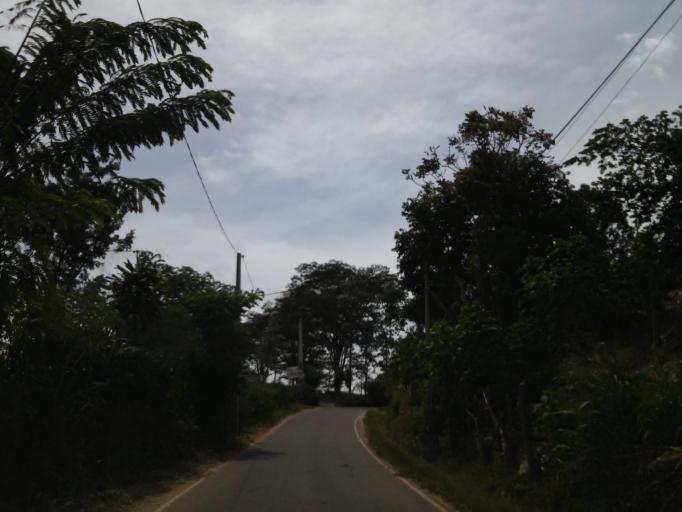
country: LK
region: Uva
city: Haputale
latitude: 6.8466
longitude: 81.0189
